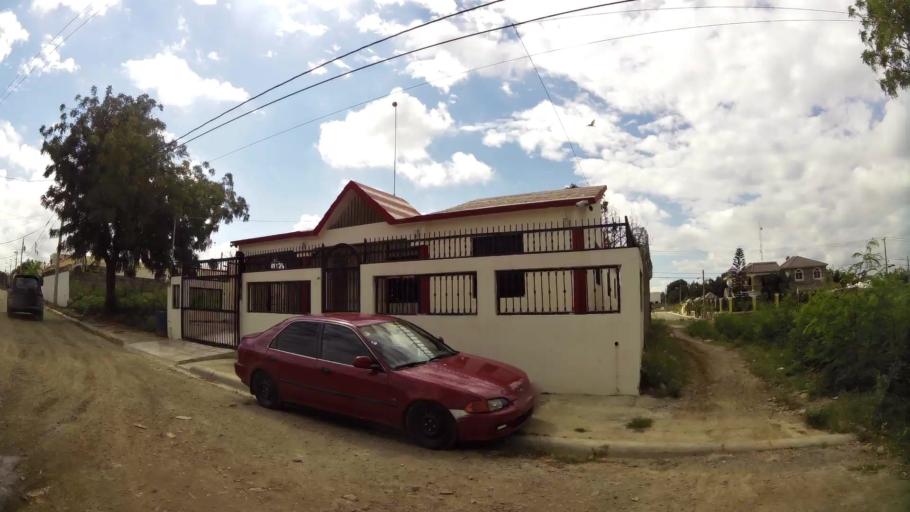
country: DO
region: Santiago
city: Palmar Arriba
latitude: 19.4906
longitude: -70.7302
